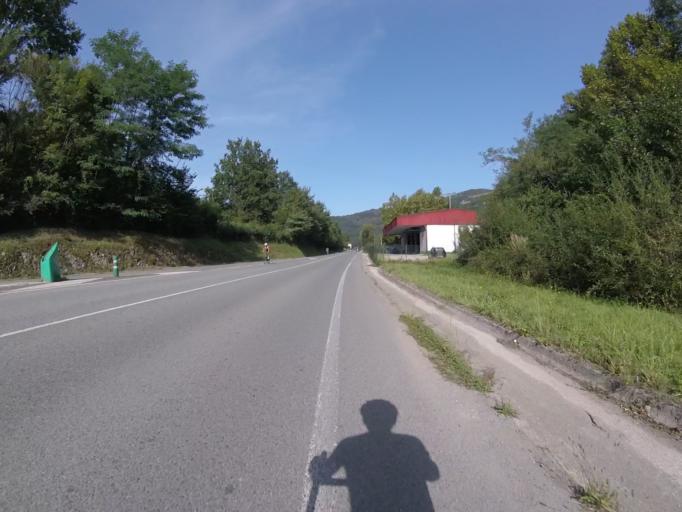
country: ES
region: Navarre
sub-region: Provincia de Navarra
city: Doneztebe
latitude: 43.1377
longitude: -1.5567
